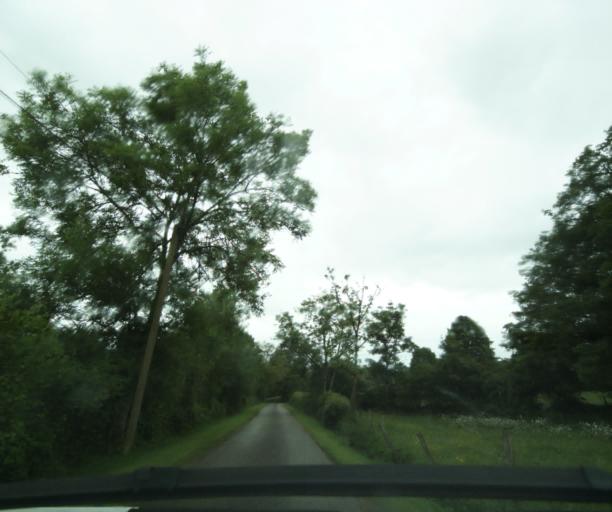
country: FR
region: Bourgogne
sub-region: Departement de Saone-et-Loire
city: Charolles
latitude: 46.5016
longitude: 4.3006
